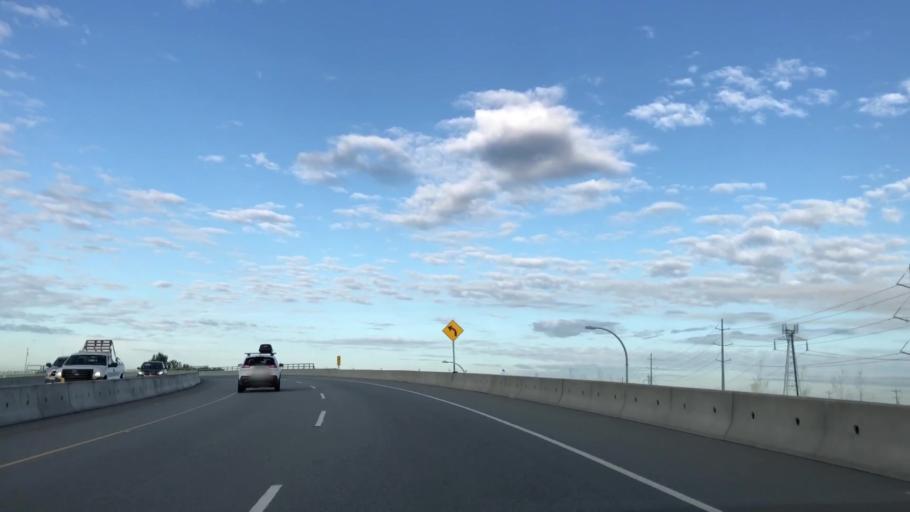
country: CA
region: British Columbia
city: Ladner
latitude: 49.0599
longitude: -123.0523
